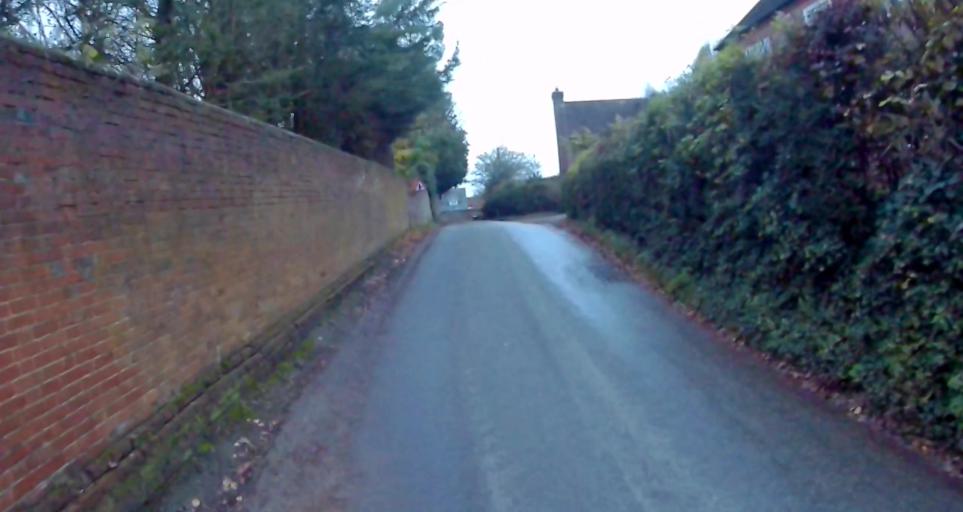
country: GB
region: England
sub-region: Hampshire
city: Old Basing
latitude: 51.2326
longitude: -1.0050
